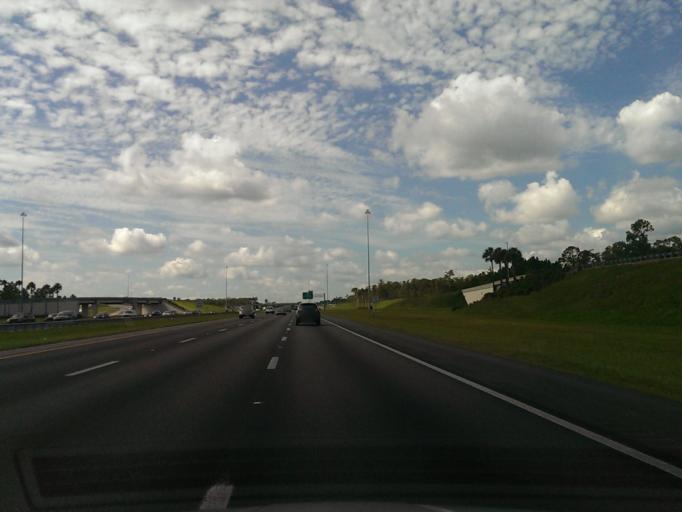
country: US
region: Florida
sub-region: Osceola County
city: Celebration
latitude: 28.3539
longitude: -81.5261
